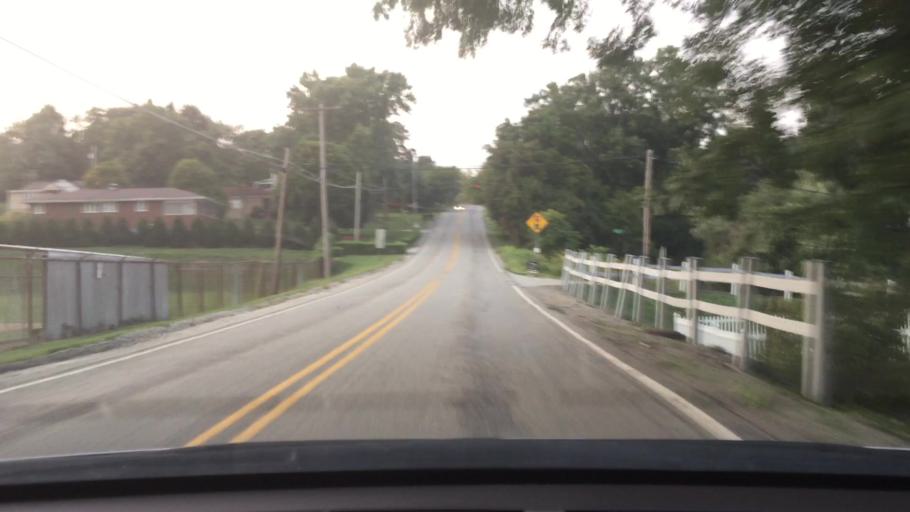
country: US
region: Pennsylvania
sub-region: Westmoreland County
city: Fellsburg
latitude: 40.1823
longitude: -79.8242
